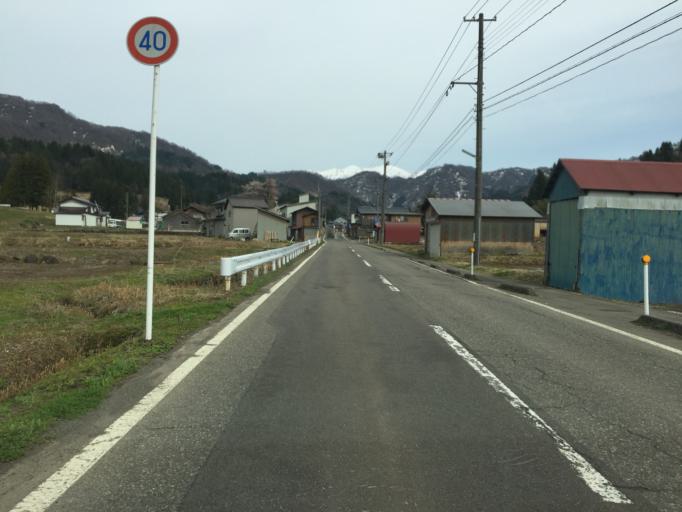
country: JP
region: Niigata
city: Tochio-honcho
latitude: 37.4453
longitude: 139.0250
